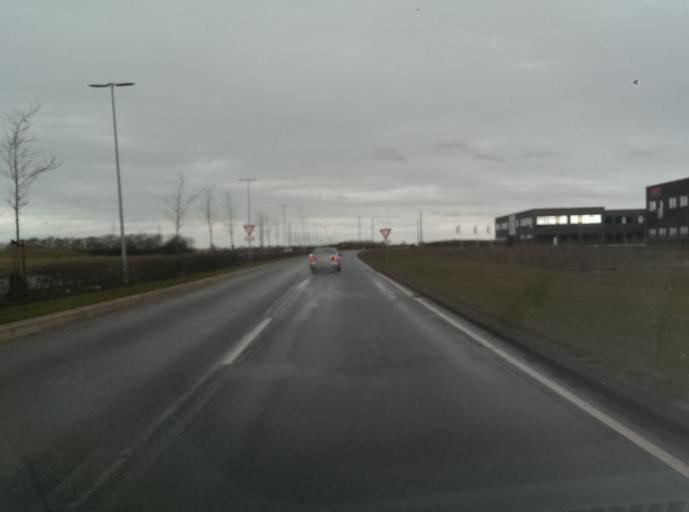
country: DK
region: South Denmark
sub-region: Esbjerg Kommune
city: Esbjerg
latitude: 55.5102
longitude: 8.4898
